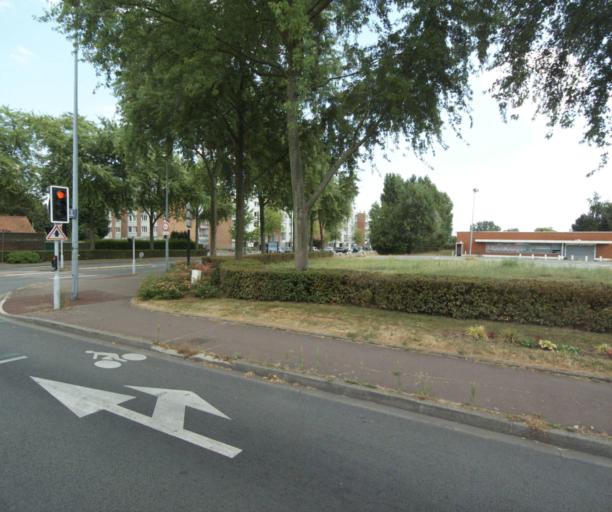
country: FR
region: Nord-Pas-de-Calais
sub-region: Departement du Nord
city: Neuville-en-Ferrain
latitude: 50.7455
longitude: 3.1754
